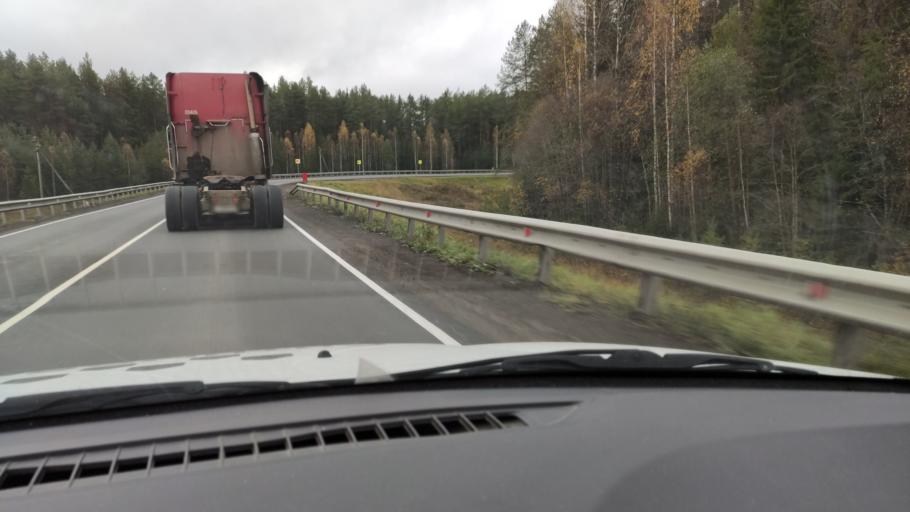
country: RU
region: Kirov
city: Belaya Kholunitsa
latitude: 58.8344
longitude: 50.6901
